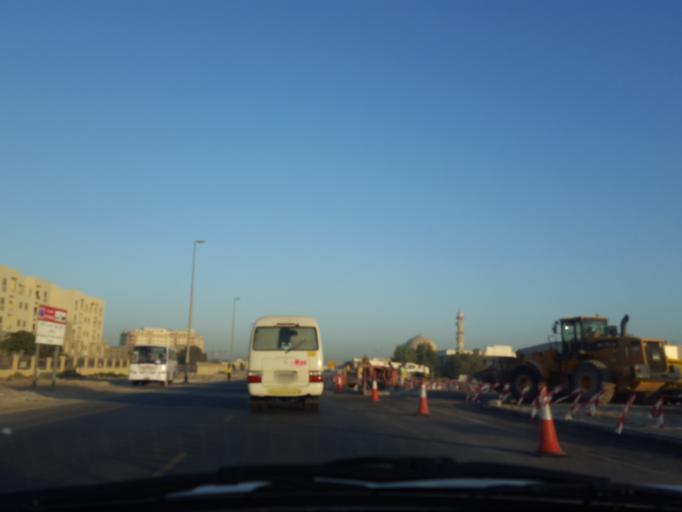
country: AE
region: Dubai
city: Dubai
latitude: 25.1411
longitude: 55.2566
